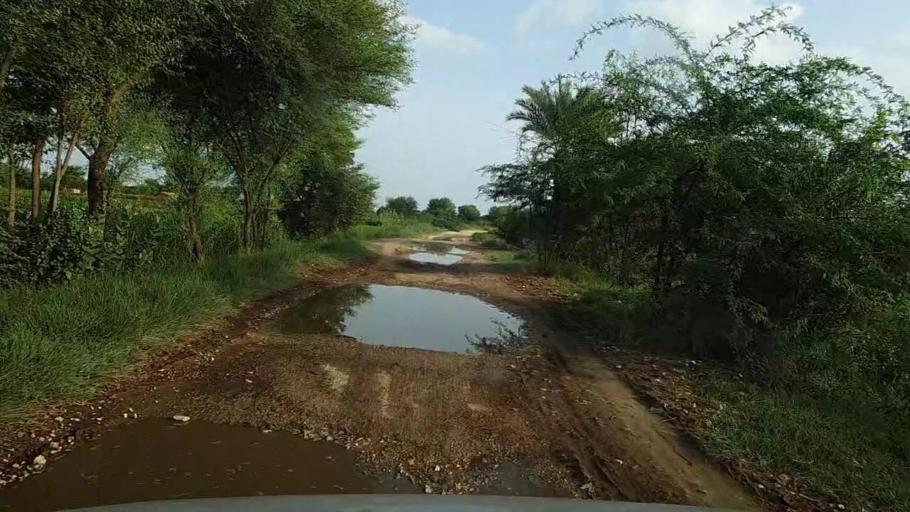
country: PK
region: Sindh
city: Pad Idan
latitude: 26.7852
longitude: 68.2206
